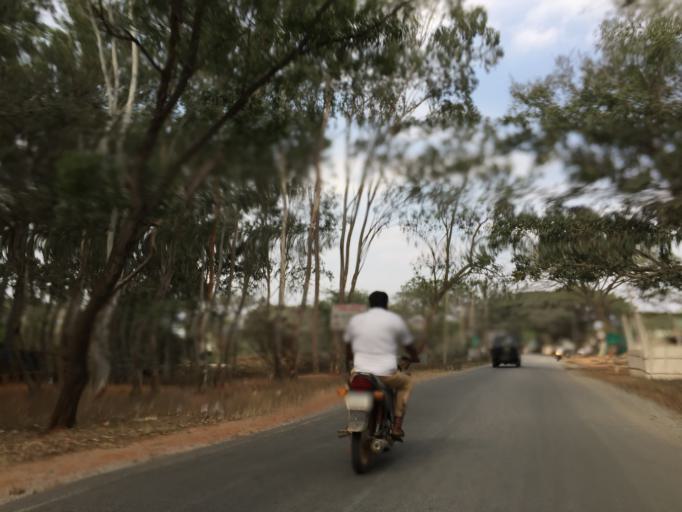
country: IN
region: Karnataka
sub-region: Chikkaballapur
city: Chik Ballapur
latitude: 13.4011
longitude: 77.7076
